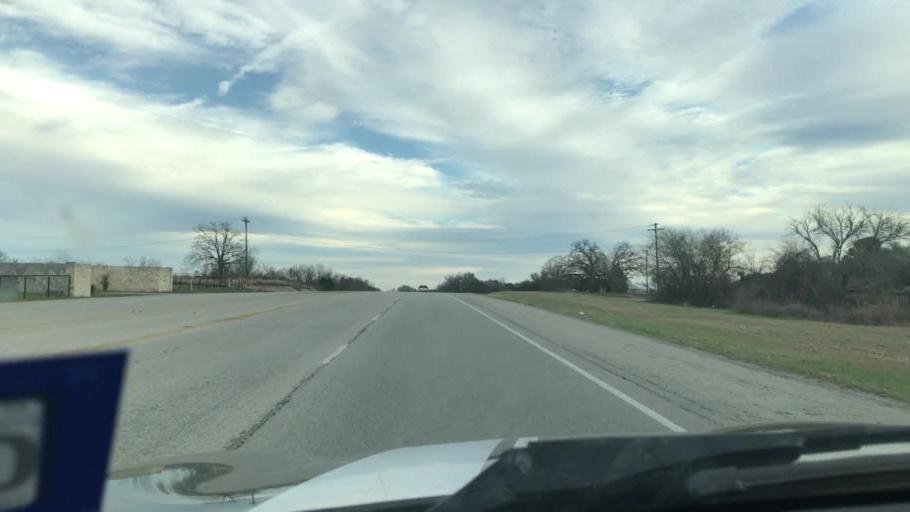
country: US
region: Texas
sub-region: Bastrop County
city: Camp Swift
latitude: 30.2894
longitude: -97.2516
